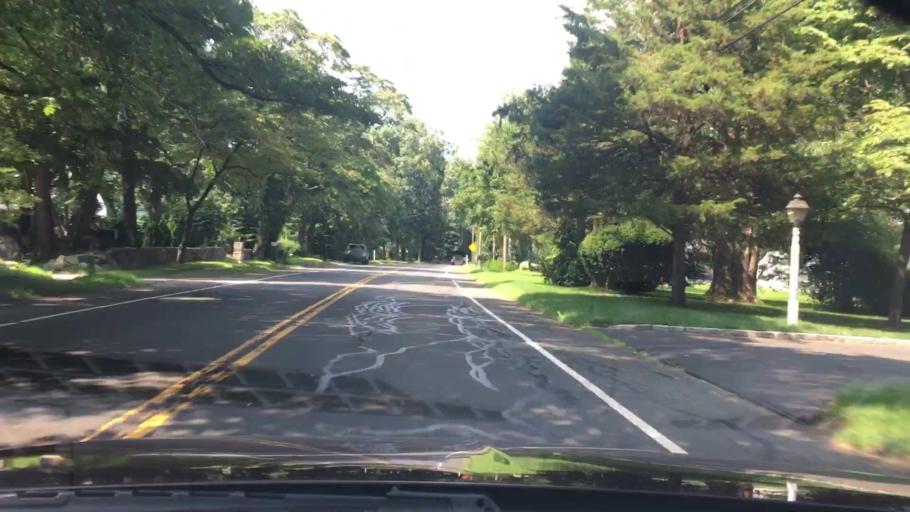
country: US
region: Connecticut
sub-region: Fairfield County
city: Norwalk
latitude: 41.1390
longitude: -73.4168
